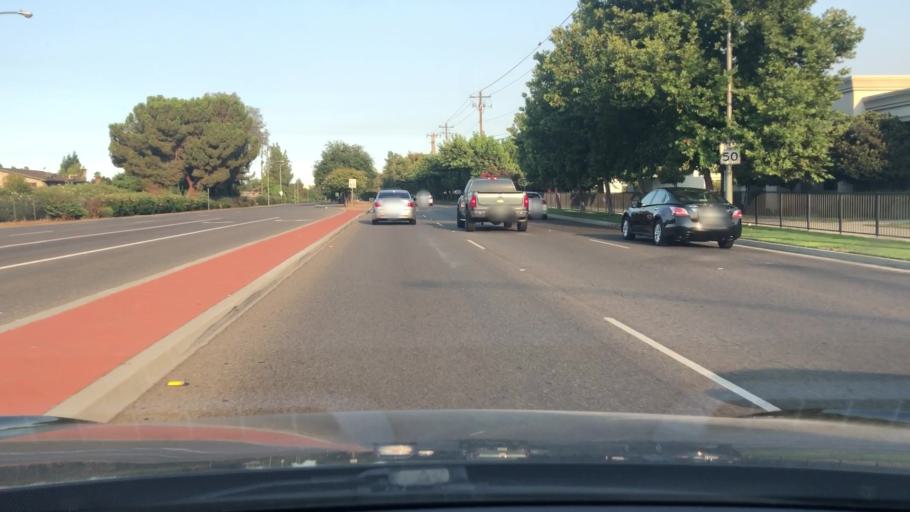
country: US
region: California
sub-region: Fresno County
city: Clovis
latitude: 36.8377
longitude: -119.7458
